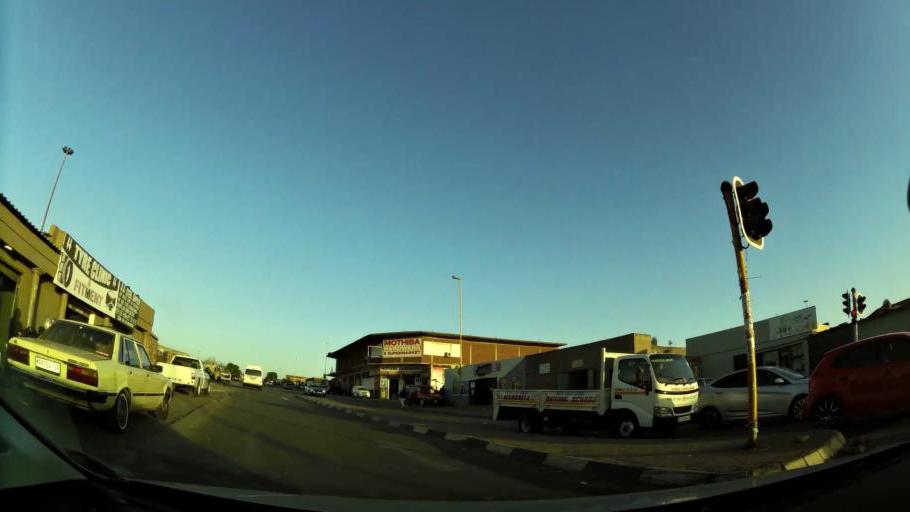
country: ZA
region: Gauteng
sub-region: Ekurhuleni Metropolitan Municipality
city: Tembisa
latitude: -25.9973
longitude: 28.2193
